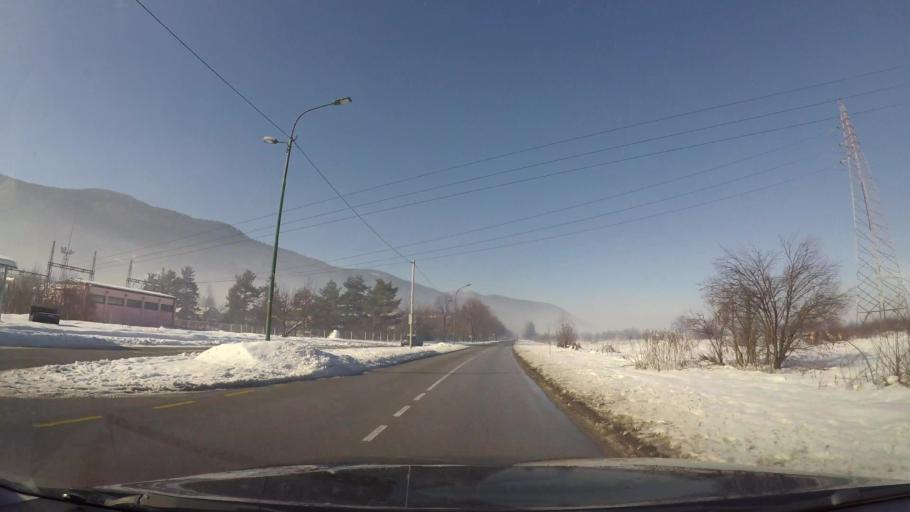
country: BA
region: Federation of Bosnia and Herzegovina
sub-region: Kanton Sarajevo
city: Sarajevo
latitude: 43.7942
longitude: 18.3254
